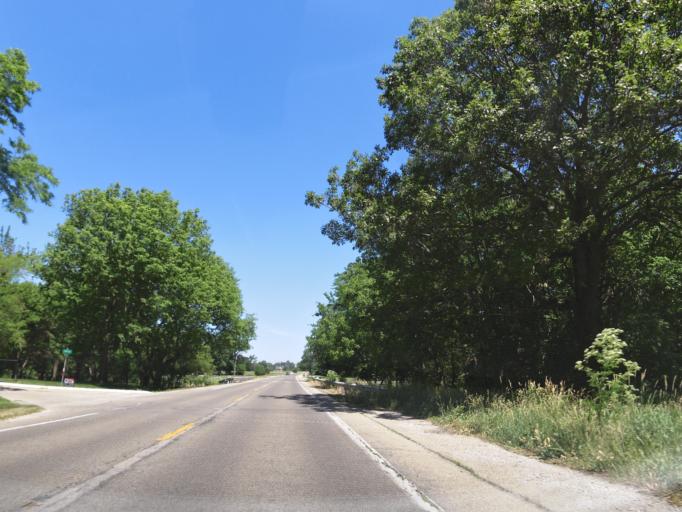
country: US
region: Illinois
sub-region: Vermilion County
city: Rossville
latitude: 40.4112
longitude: -87.6833
